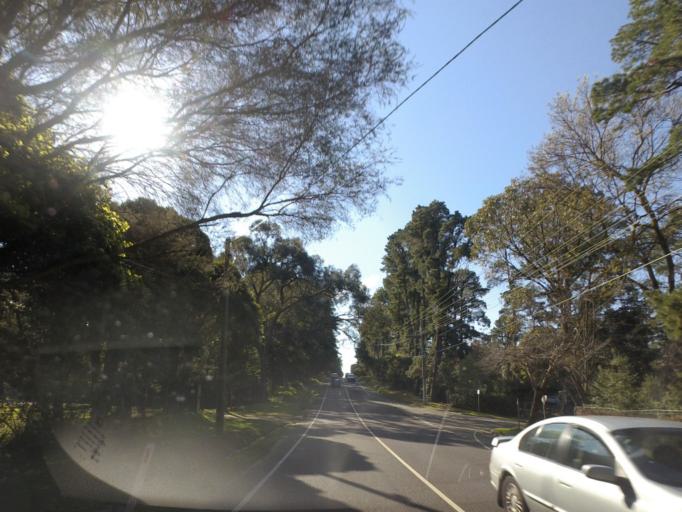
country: AU
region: Victoria
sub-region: Manningham
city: Donvale
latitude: -37.7910
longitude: 145.1802
